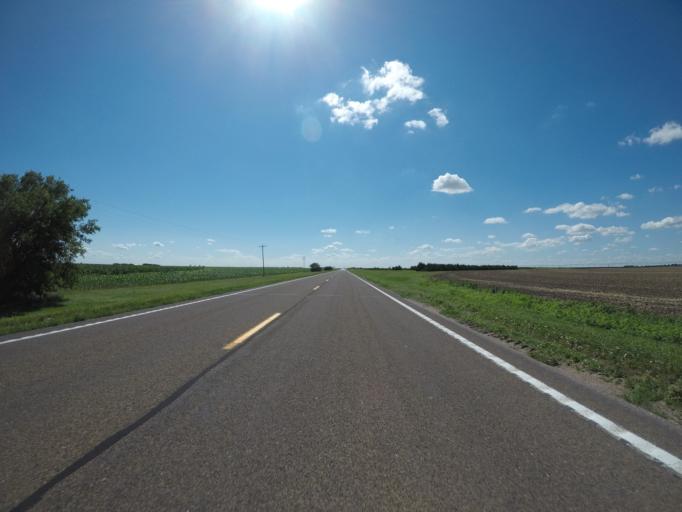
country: US
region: Nebraska
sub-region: Chase County
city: Imperial
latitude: 40.5377
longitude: -101.8803
